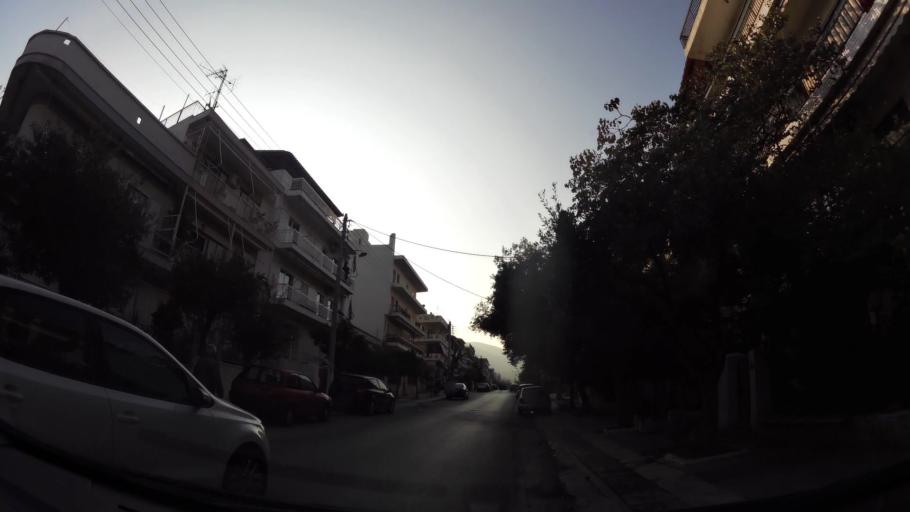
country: GR
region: Attica
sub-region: Nomarchia Athinas
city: Ymittos
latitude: 37.9410
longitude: 23.7554
